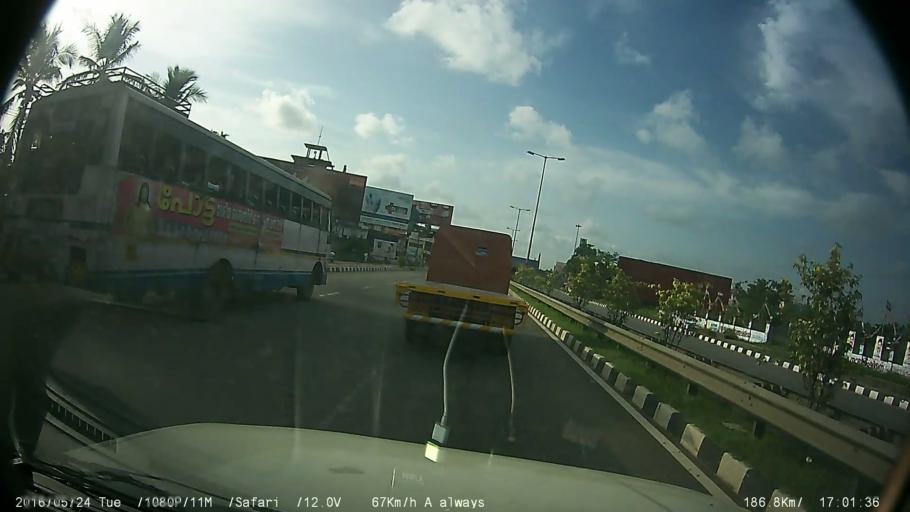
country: IN
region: Kerala
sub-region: Thrissur District
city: Trichur
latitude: 10.4311
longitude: 76.2673
